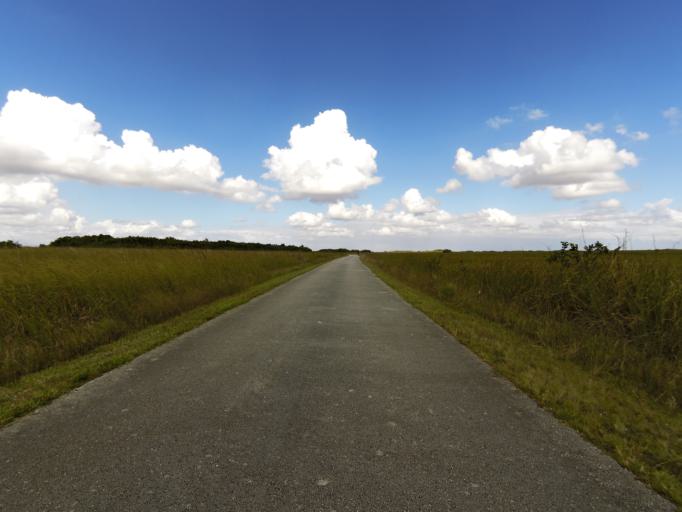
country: US
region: Florida
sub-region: Miami-Dade County
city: The Hammocks
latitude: 25.6690
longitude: -80.7607
